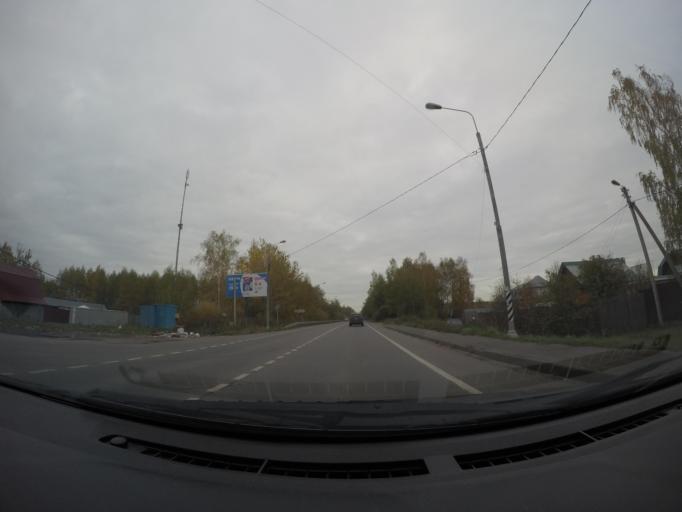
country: RU
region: Moskovskaya
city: Elektrougli
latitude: 55.7263
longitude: 38.2589
